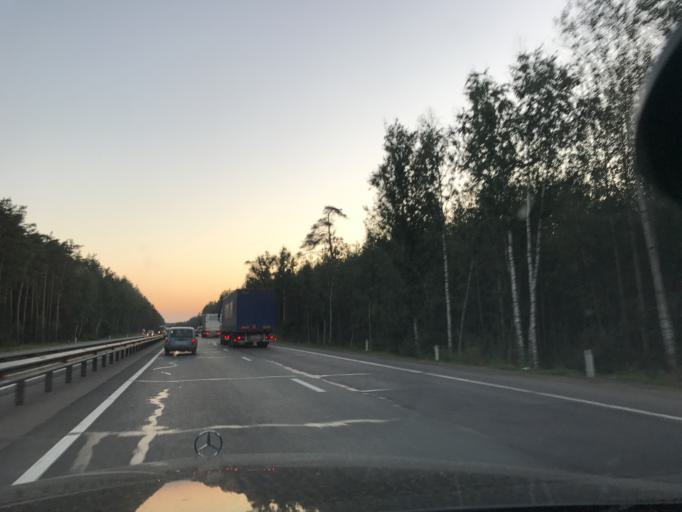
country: RU
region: Moskovskaya
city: Malaya Dubna
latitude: 55.8720
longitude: 38.9428
